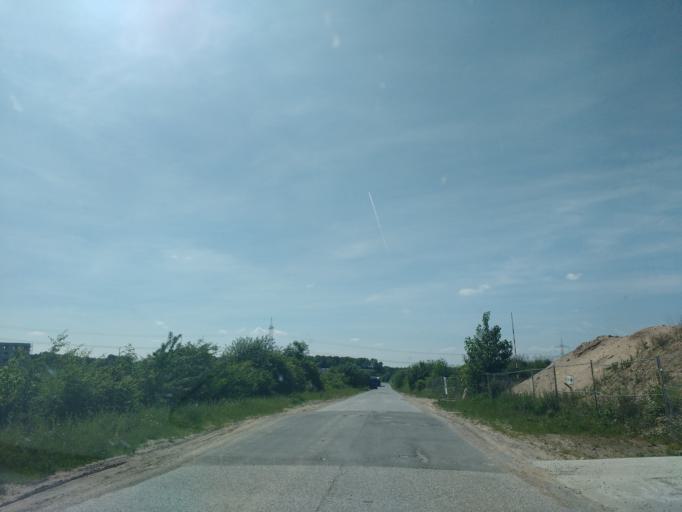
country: DE
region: North Rhine-Westphalia
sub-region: Regierungsbezirk Detmold
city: Paderborn
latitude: 51.6882
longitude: 8.7210
